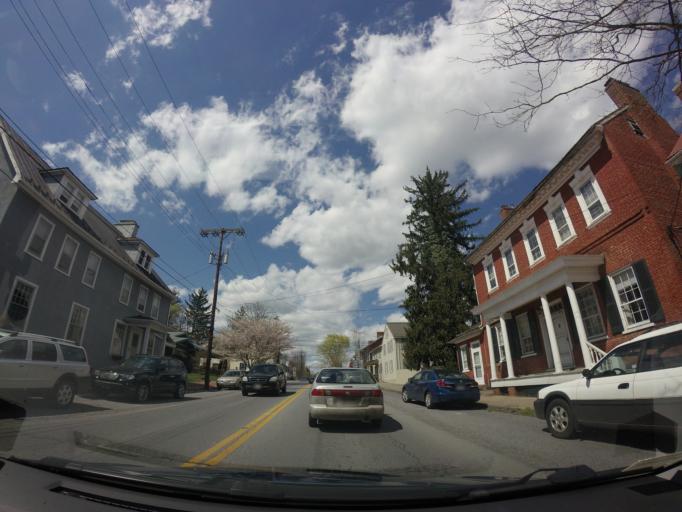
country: US
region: West Virginia
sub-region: Jefferson County
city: Shepherdstown
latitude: 39.4318
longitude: -77.8083
